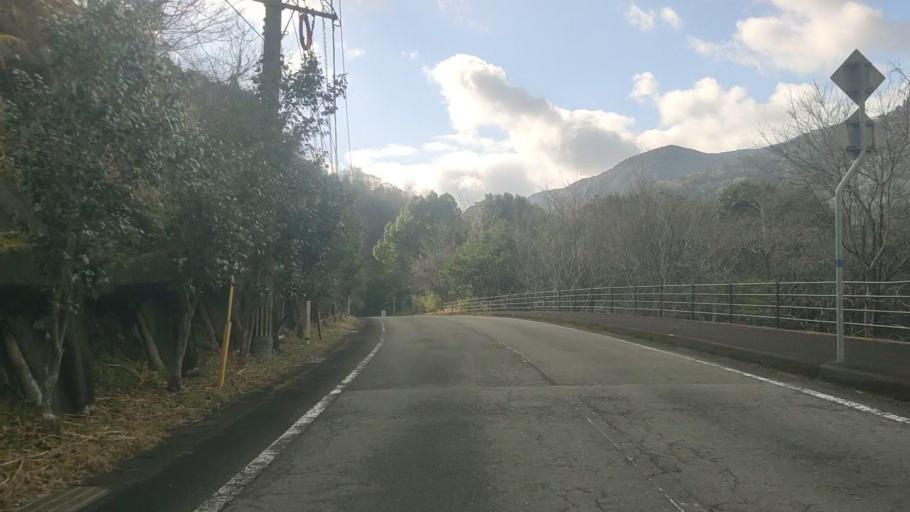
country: JP
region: Kumamoto
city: Hitoyoshi
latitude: 32.3844
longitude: 130.8348
